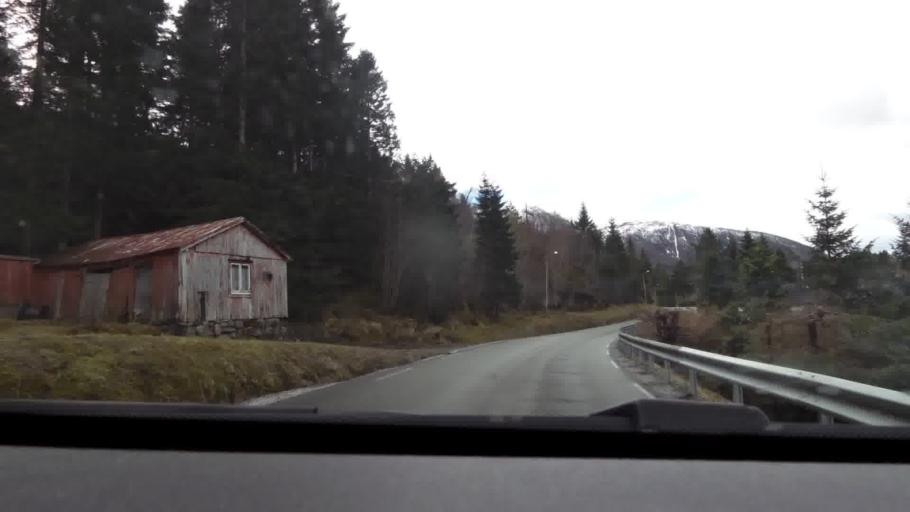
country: NO
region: More og Romsdal
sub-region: Eide
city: Eide
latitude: 62.9163
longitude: 7.5492
